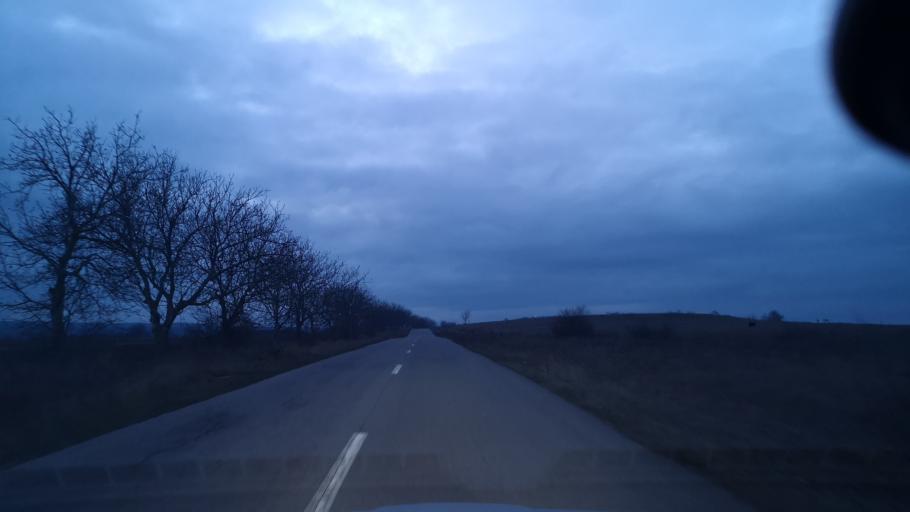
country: MD
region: Telenesti
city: Cocieri
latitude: 47.3074
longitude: 28.9848
